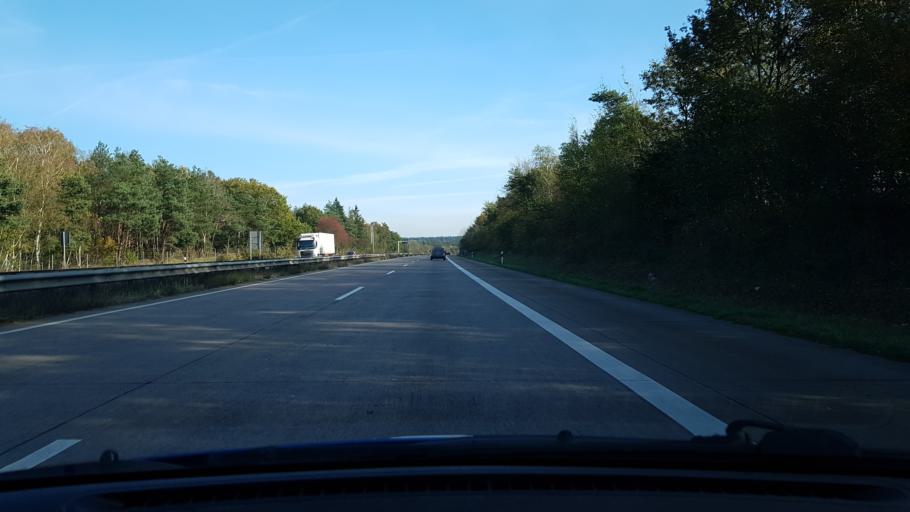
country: DE
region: Schleswig-Holstein
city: Guster
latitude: 53.5518
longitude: 10.6640
